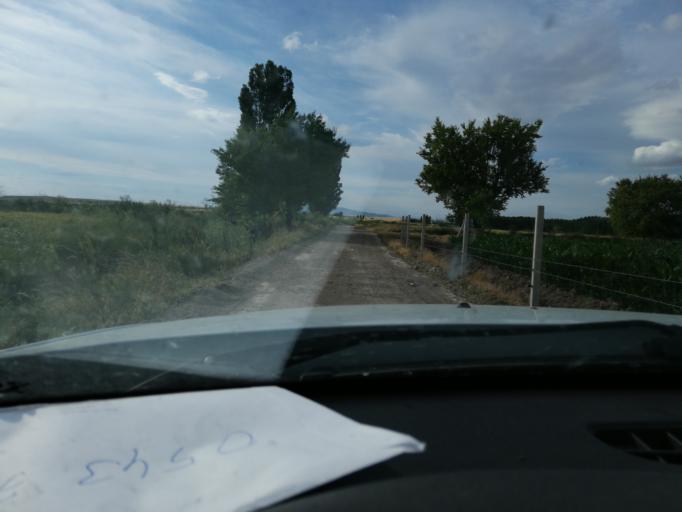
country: TR
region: Kirsehir
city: Kirsehir
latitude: 38.9971
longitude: 34.1253
